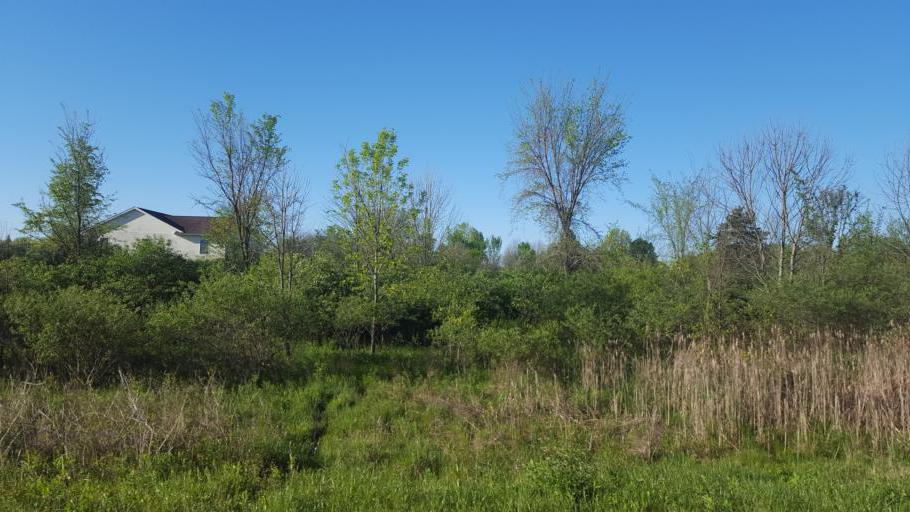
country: US
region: Ohio
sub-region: Delaware County
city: Sunbury
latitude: 40.3390
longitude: -82.8336
